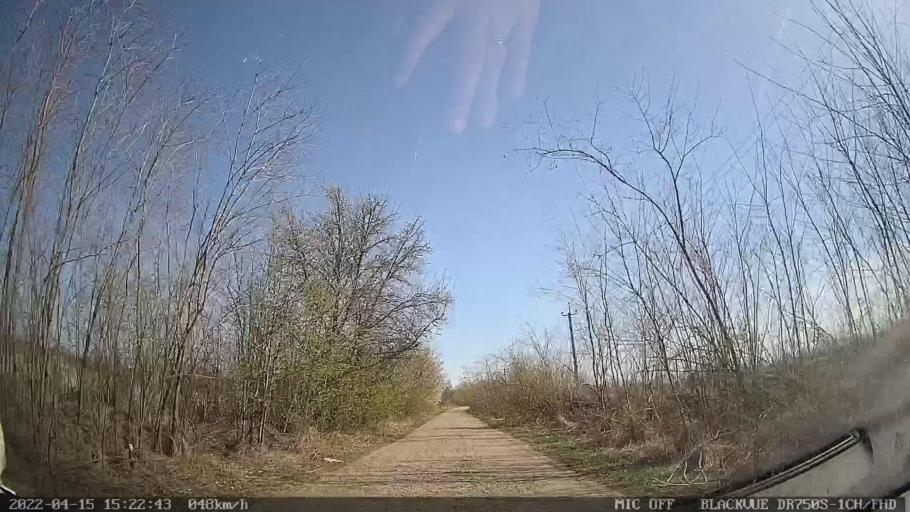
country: MD
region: Raionul Ocnita
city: Otaci
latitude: 48.3794
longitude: 27.9156
